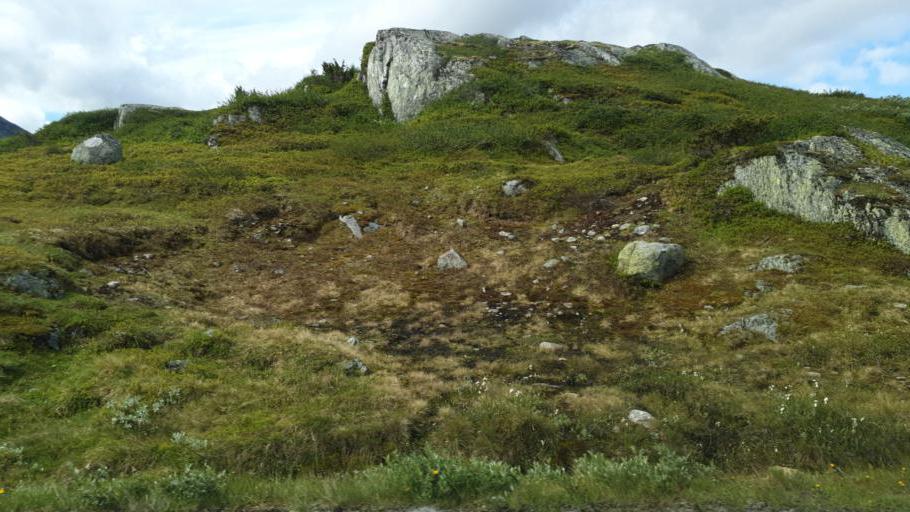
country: NO
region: Oppland
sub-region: Vestre Slidre
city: Slidre
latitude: 61.3254
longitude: 8.8043
